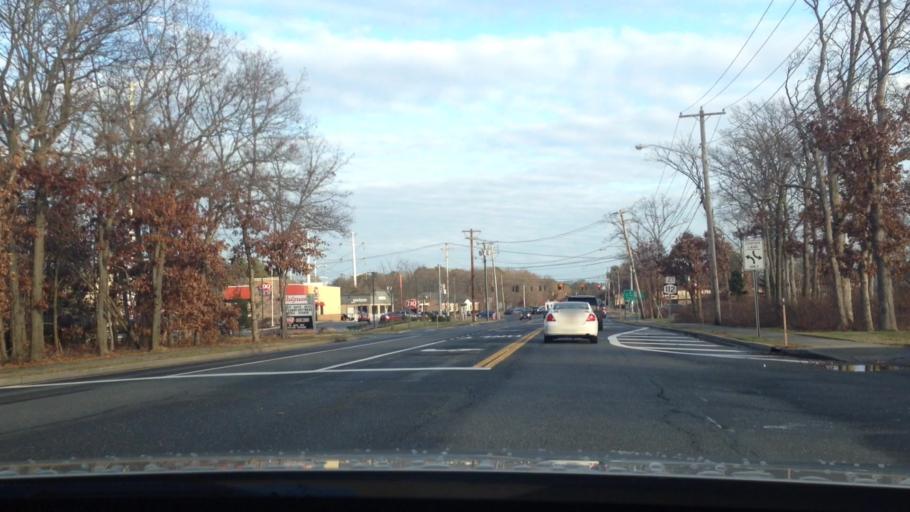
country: US
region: New York
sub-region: Suffolk County
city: Medford
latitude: 40.8276
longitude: -72.9974
